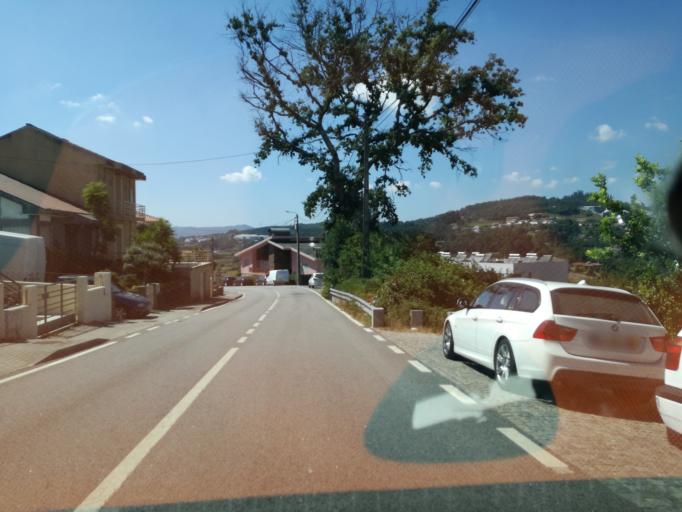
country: PT
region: Braga
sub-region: Guimaraes
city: Guimaraes
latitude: 41.4600
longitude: -8.2844
